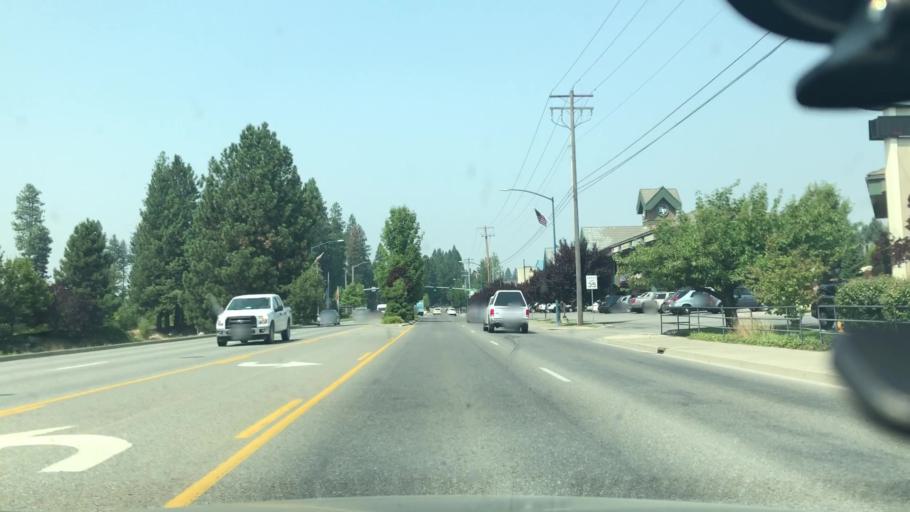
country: US
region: Idaho
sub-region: Kootenai County
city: Coeur d'Alene
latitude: 47.6812
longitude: -116.7925
